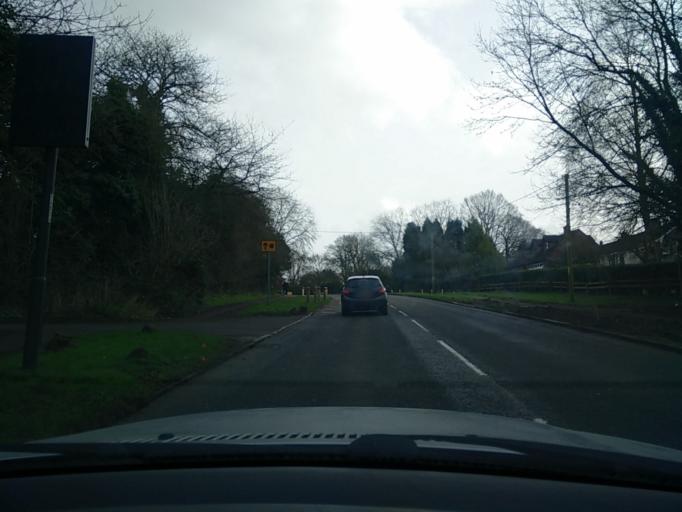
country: GB
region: England
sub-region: Buckinghamshire
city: High Wycombe
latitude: 51.6641
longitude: -0.7387
